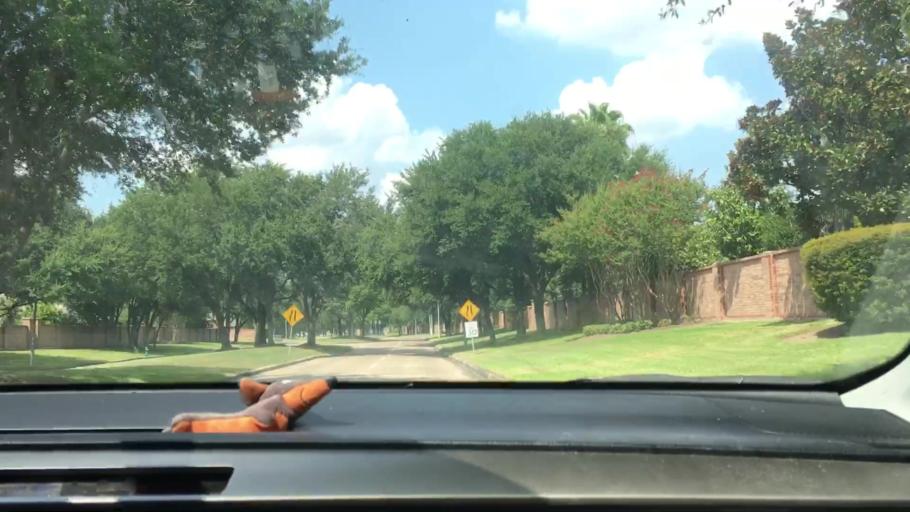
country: US
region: Texas
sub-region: Fort Bend County
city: Meadows Place
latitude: 29.7246
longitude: -95.5947
